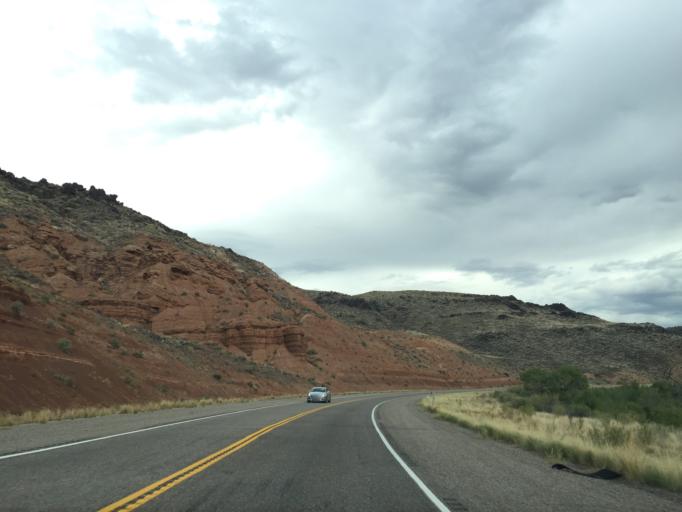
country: US
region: Utah
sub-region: Washington County
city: LaVerkin
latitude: 37.1787
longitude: -113.1184
